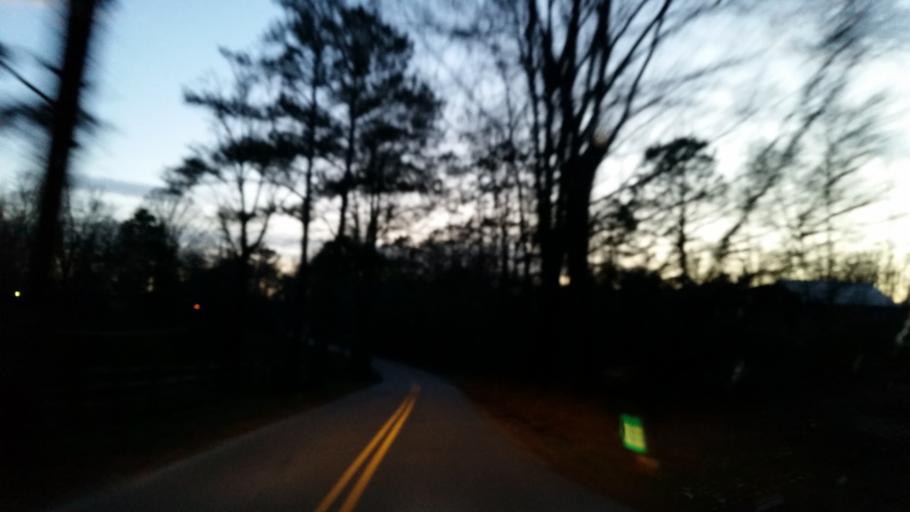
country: US
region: Georgia
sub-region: Cherokee County
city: Ball Ground
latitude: 34.3036
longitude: -84.4417
